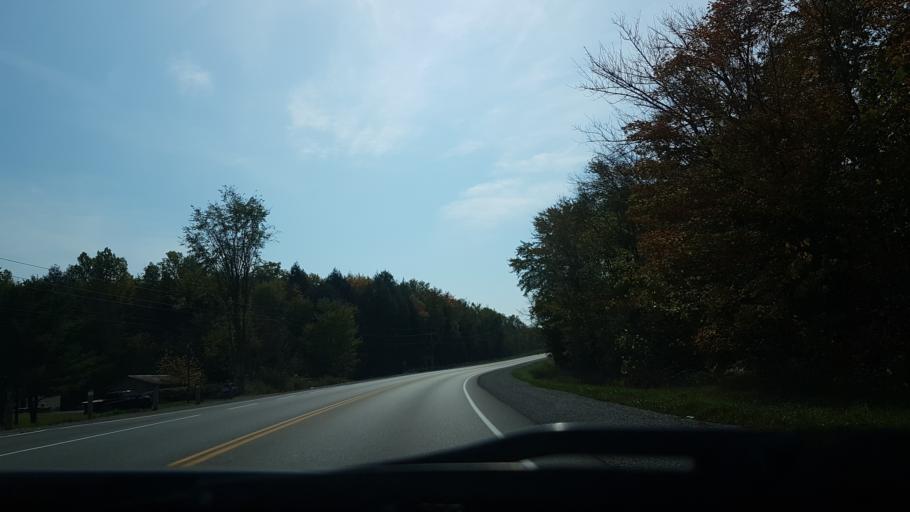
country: CA
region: Ontario
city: Orillia
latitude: 44.7381
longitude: -79.2922
